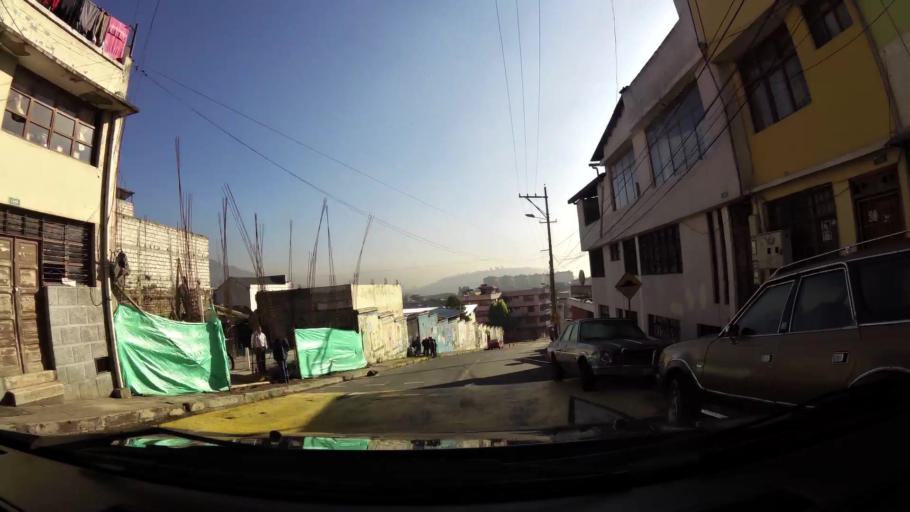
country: EC
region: Pichincha
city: Quito
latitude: -0.2425
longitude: -78.5140
